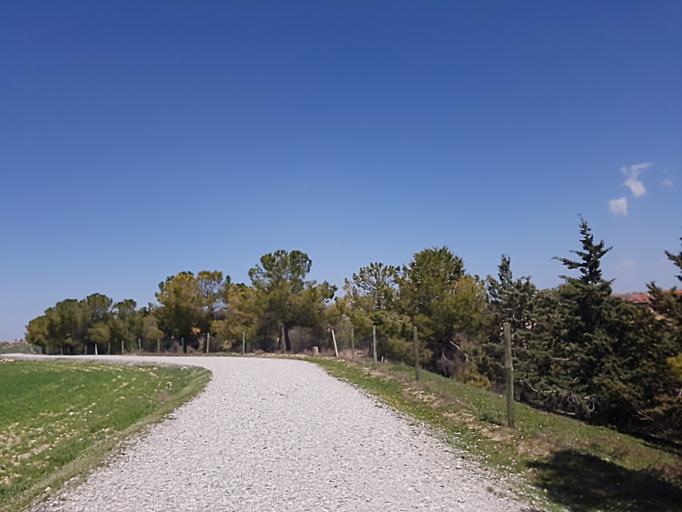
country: ES
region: Castille and Leon
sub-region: Provincia de Segovia
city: Segovia
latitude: 40.9496
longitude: -4.1343
